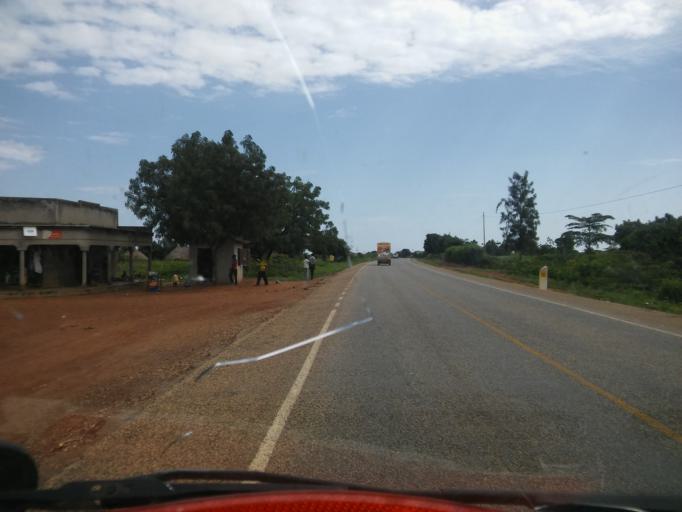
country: UG
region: Eastern Region
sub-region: Bukedea District
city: Bukedea
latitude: 1.2679
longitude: 34.0861
